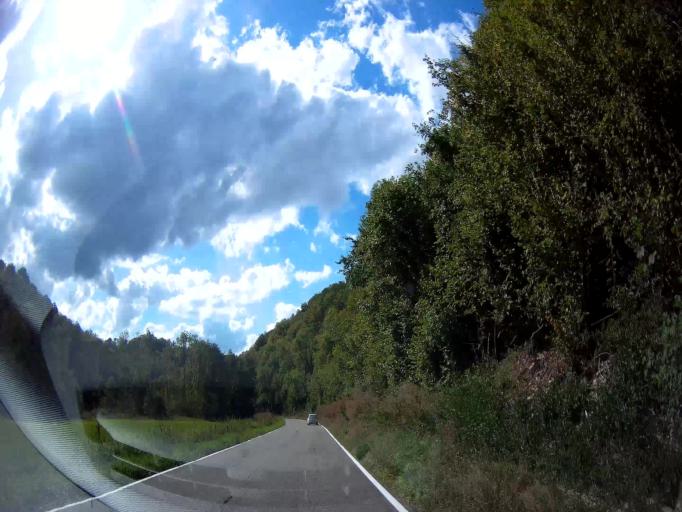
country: BE
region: Wallonia
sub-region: Province de Namur
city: Anhee
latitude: 50.3036
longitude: 4.8256
